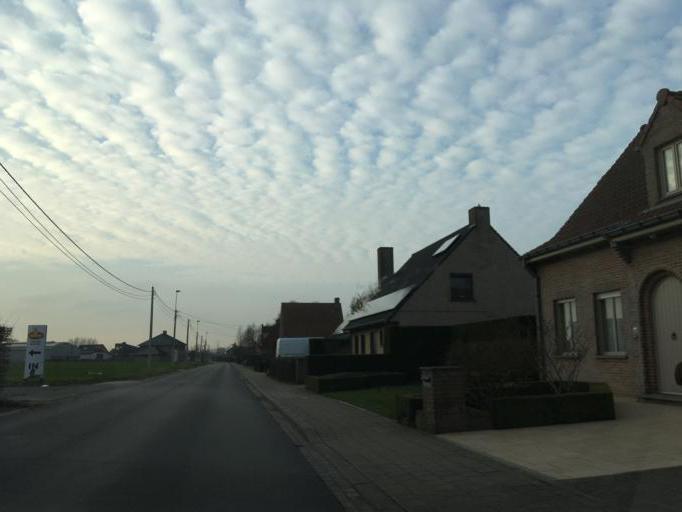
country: BE
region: Flanders
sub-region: Provincie West-Vlaanderen
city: Roeselare
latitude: 50.9288
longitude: 3.1145
